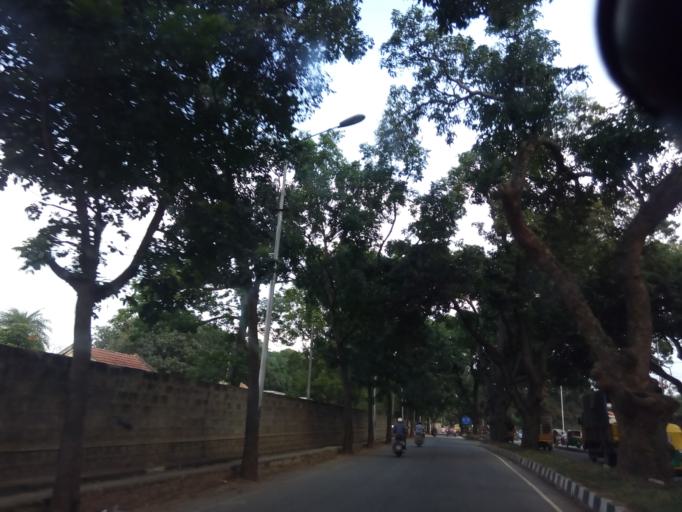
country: IN
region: Karnataka
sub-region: Bangalore Urban
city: Bangalore
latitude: 13.0120
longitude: 77.5893
